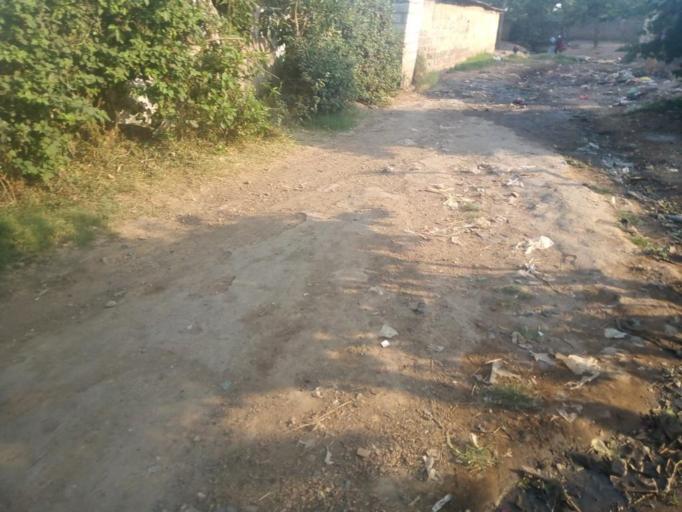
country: ZM
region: Lusaka
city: Lusaka
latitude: -15.4039
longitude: 28.3645
